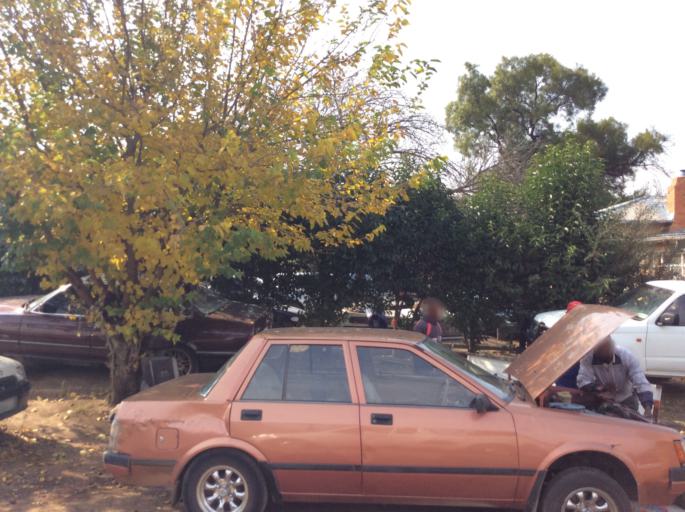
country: LS
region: Mafeteng
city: Mafeteng
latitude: -29.7251
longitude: 27.0433
